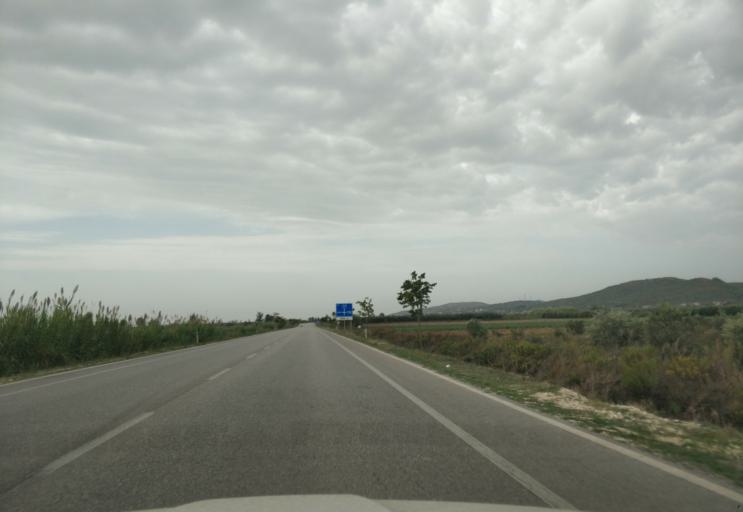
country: AL
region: Fier
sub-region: Rrethi i Fierit
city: Frakulla e Madhe
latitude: 40.6497
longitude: 19.4955
